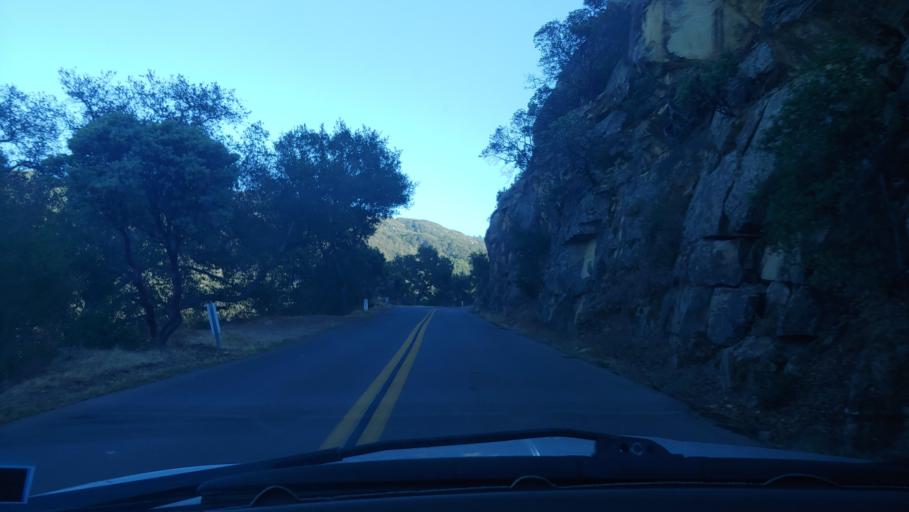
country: US
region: California
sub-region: Santa Barbara County
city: Goleta
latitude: 34.5295
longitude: -119.8345
